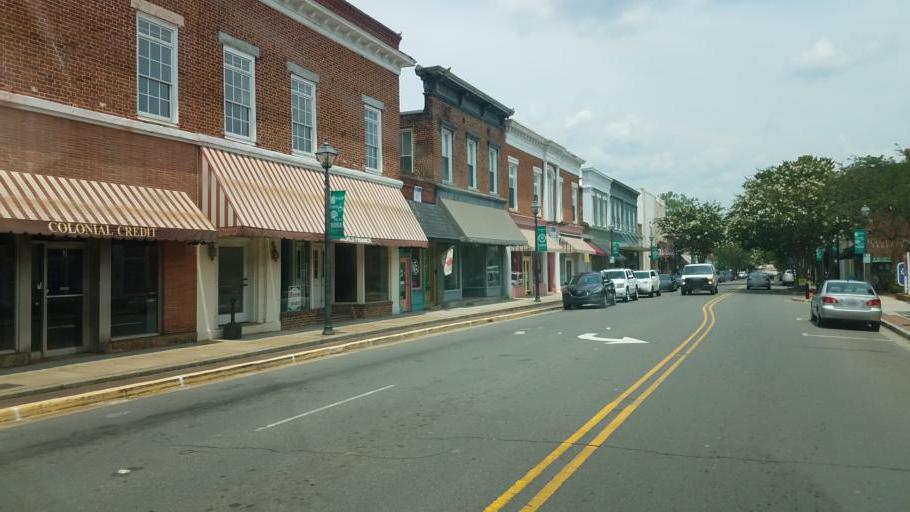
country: US
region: South Carolina
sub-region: York County
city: York
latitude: 34.9942
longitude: -81.2419
